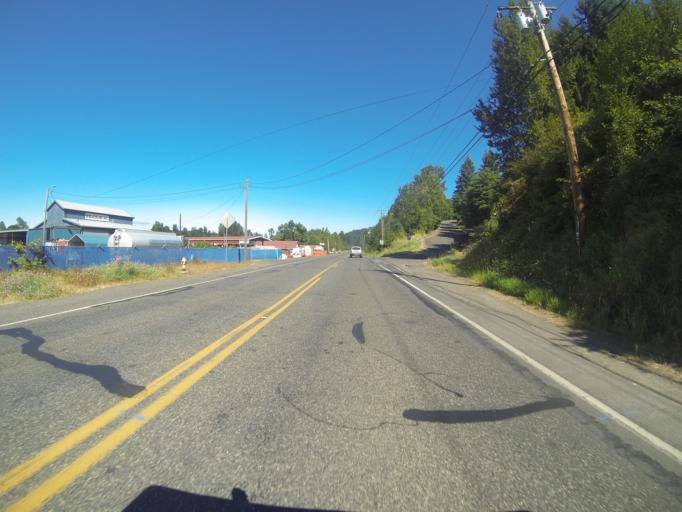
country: US
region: Washington
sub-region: Cowlitz County
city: Woodland
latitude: 45.9186
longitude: -122.7448
